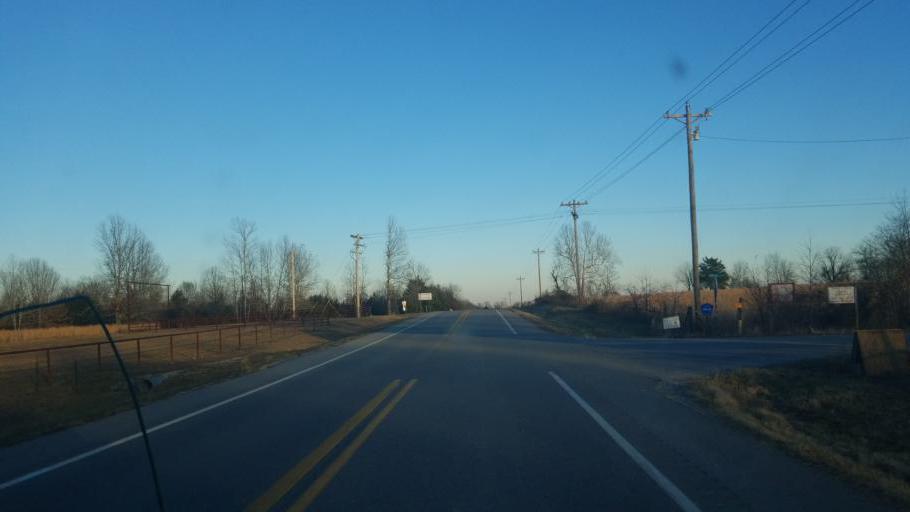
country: US
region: Arkansas
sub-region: Baxter County
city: Mountain Home
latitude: 36.3757
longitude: -92.1467
